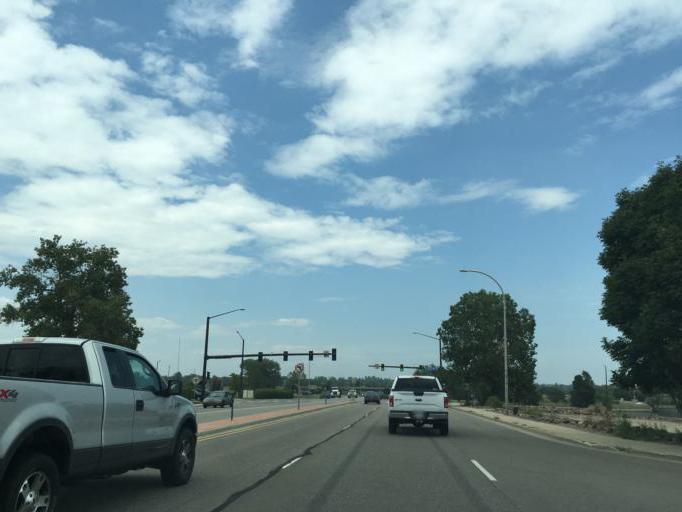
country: US
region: Colorado
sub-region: Jefferson County
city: Lakewood
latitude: 39.7215
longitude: -105.1096
